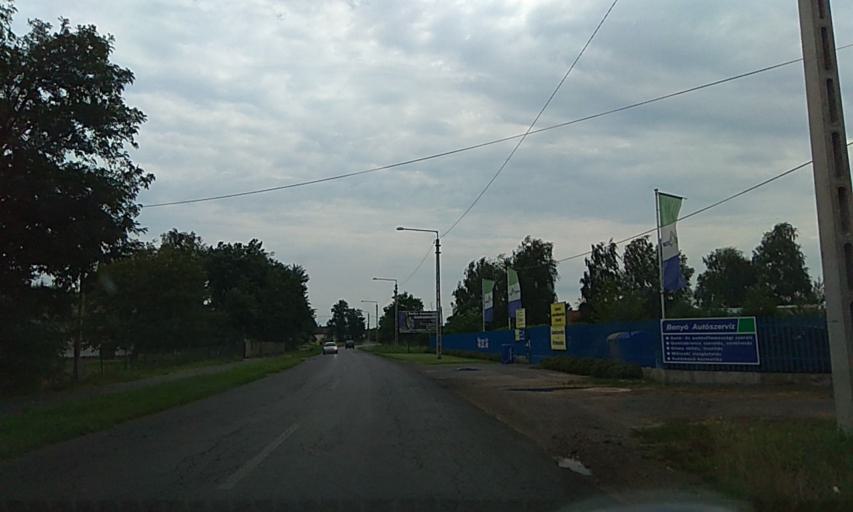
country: HU
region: Szabolcs-Szatmar-Bereg
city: Kotaj
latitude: 48.0127
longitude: 21.6894
